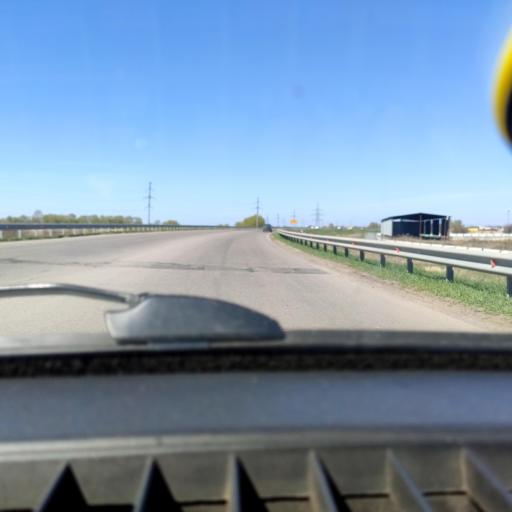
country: RU
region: Samara
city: Tol'yatti
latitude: 53.6696
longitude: 49.4149
